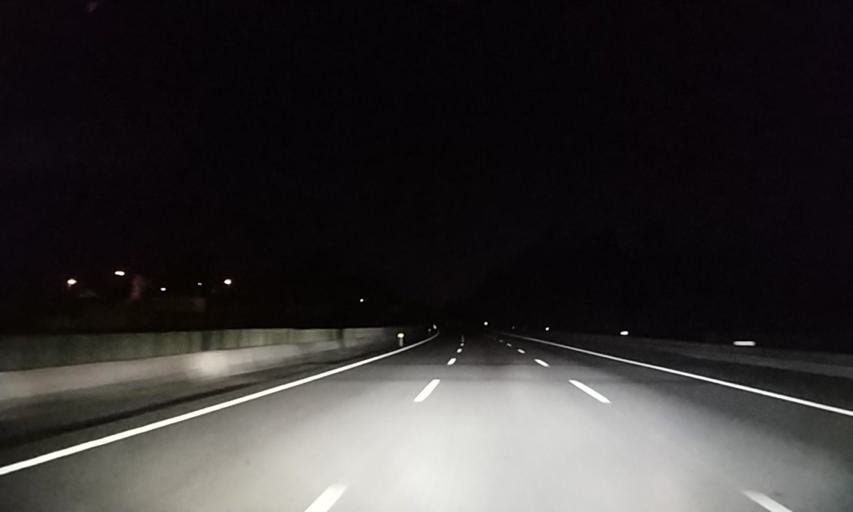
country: PT
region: Aveiro
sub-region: Ovar
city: Valega
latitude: 40.8410
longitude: -8.5553
